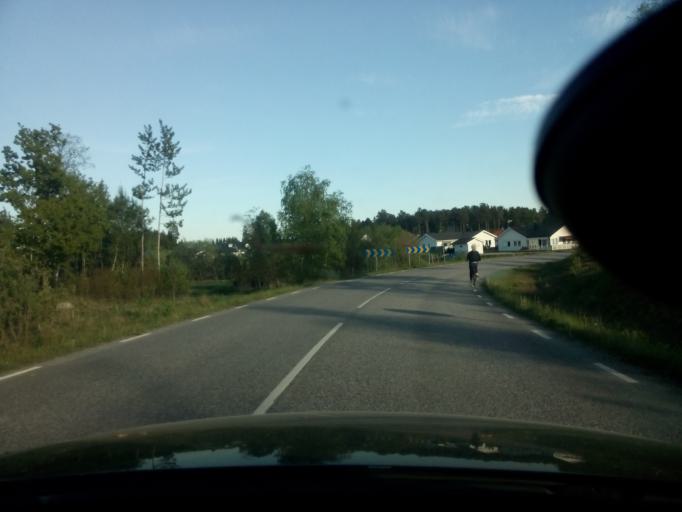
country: SE
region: Soedermanland
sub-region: Nykopings Kommun
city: Nykoping
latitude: 58.7806
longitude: 17.0065
